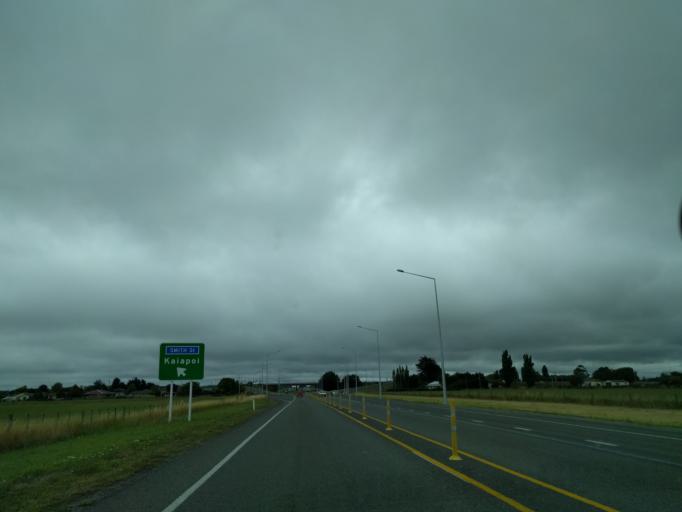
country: NZ
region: Canterbury
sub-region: Waimakariri District
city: Kaiapoi
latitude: -43.3702
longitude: 172.6486
